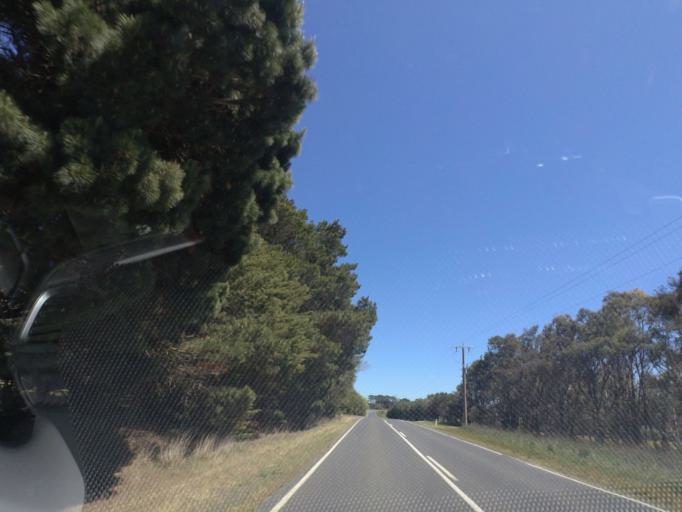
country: AU
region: Victoria
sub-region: Hume
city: Sunbury
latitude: -37.2849
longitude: 144.7619
